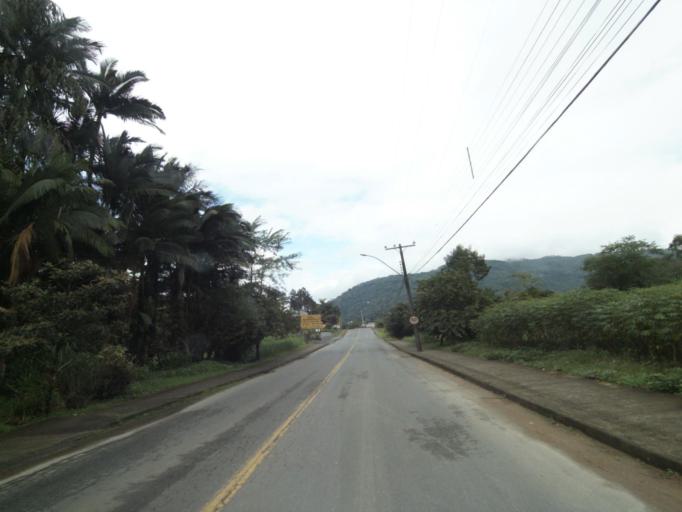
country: BR
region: Santa Catarina
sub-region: Pomerode
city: Pomerode
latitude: -26.7194
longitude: -49.1788
